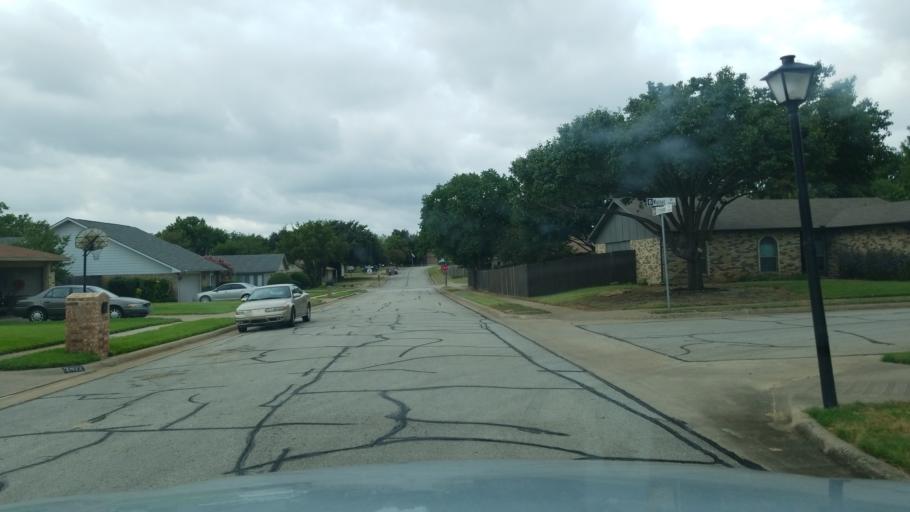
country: US
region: Texas
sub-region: Tarrant County
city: Euless
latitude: 32.8477
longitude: -97.1042
